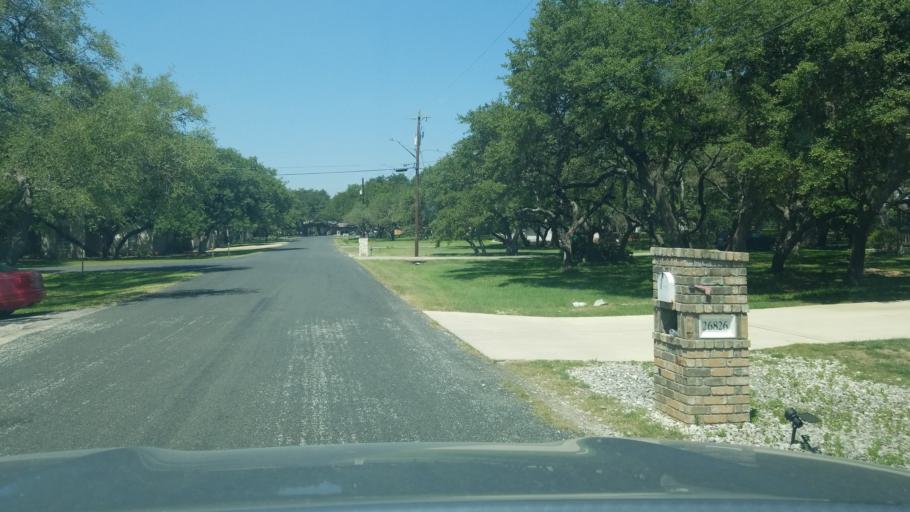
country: US
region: Texas
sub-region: Bexar County
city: Timberwood Park
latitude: 29.6995
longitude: -98.4873
